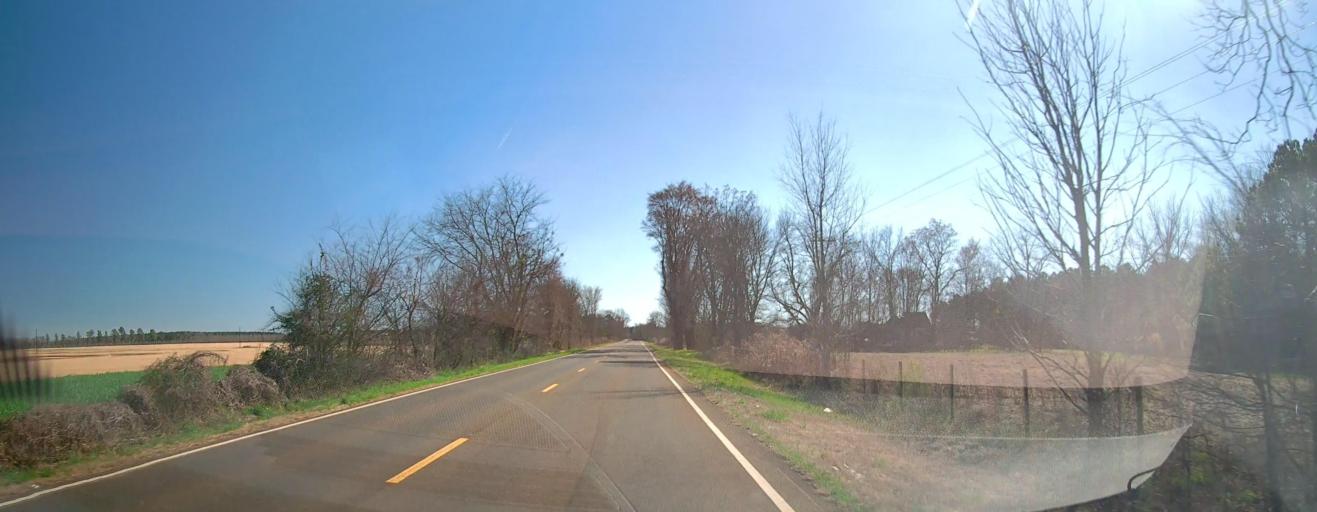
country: US
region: Georgia
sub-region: Macon County
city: Montezuma
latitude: 32.3815
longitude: -84.0151
